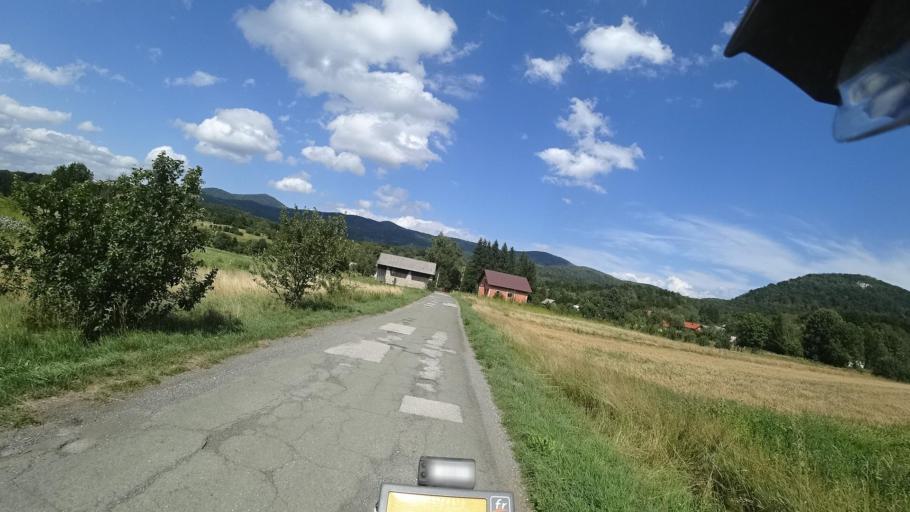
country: HR
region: Licko-Senjska
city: Brinje
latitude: 45.1166
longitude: 15.1212
